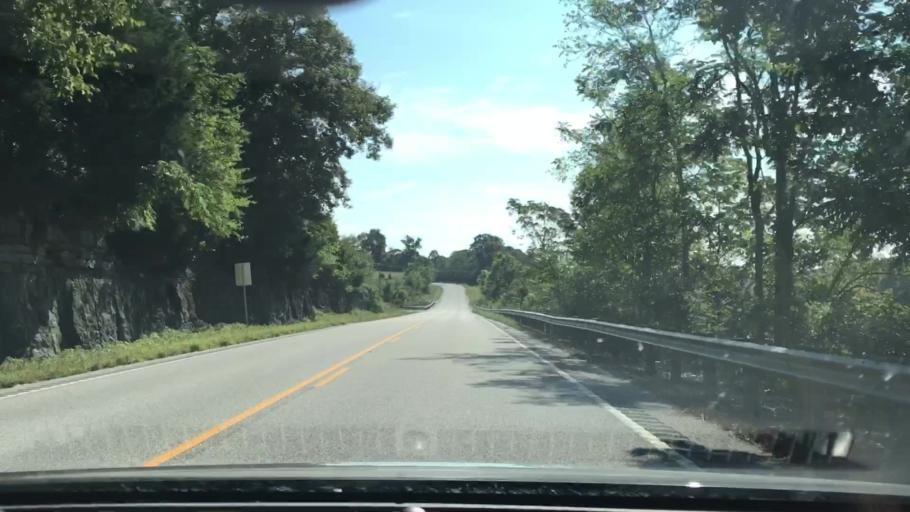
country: US
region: Tennessee
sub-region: Jackson County
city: Gainesboro
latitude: 36.3592
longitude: -85.7463
